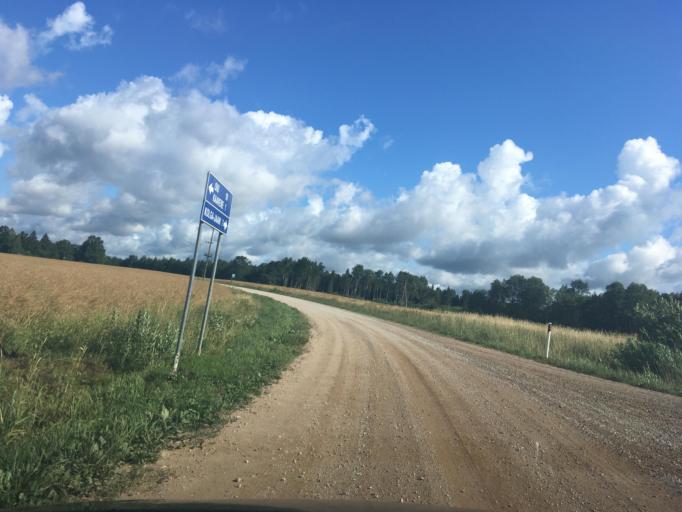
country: EE
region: Jogevamaa
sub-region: Poltsamaa linn
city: Poltsamaa
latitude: 58.4798
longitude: 25.9694
